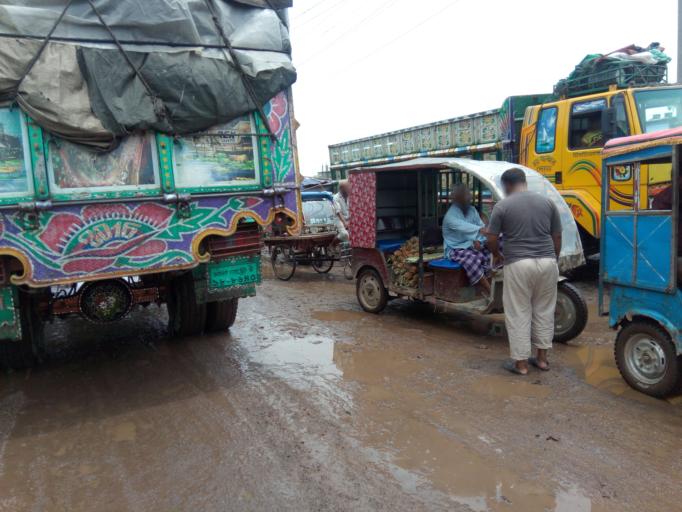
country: BD
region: Dhaka
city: Azimpur
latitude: 23.7236
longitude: 90.3727
